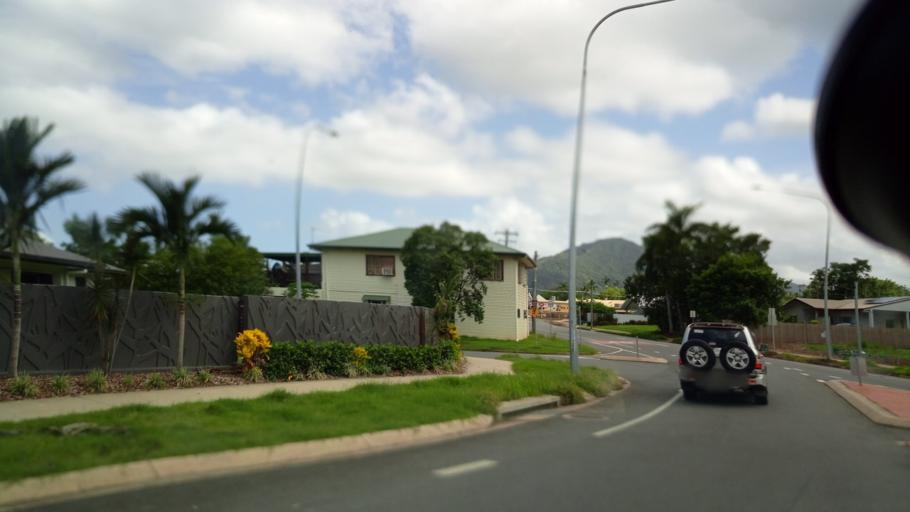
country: AU
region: Queensland
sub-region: Cairns
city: Redlynch
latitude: -16.8861
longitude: 145.6953
